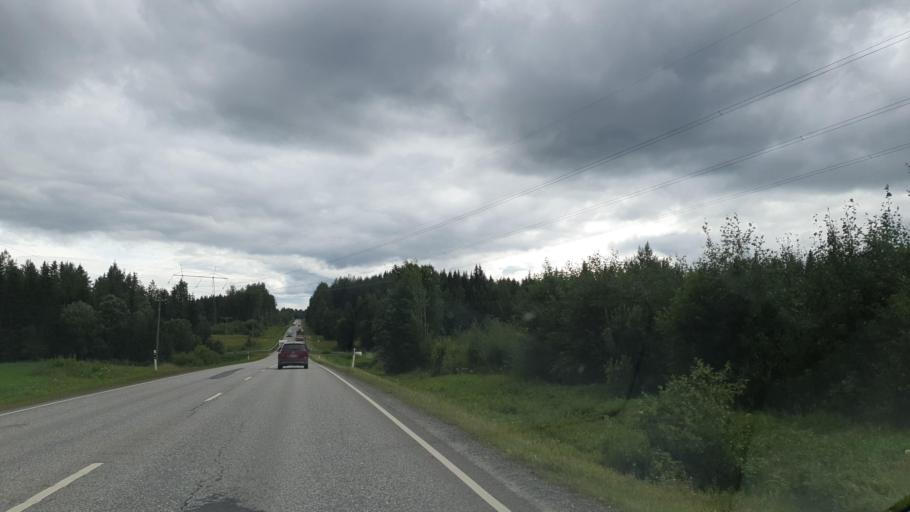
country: FI
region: Northern Savo
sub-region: Ylae-Savo
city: Sonkajaervi
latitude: 63.7083
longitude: 27.3584
